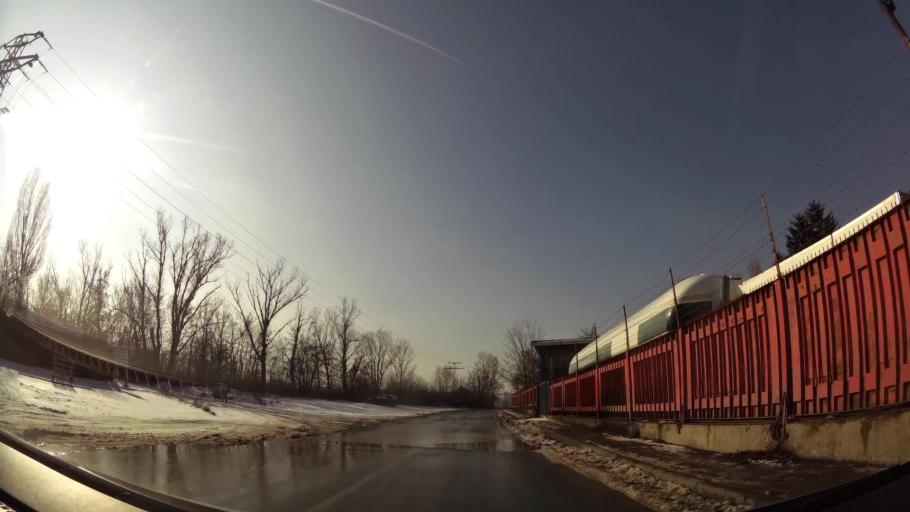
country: BG
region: Sofia-Capital
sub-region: Stolichna Obshtina
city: Sofia
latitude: 42.6568
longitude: 23.3265
